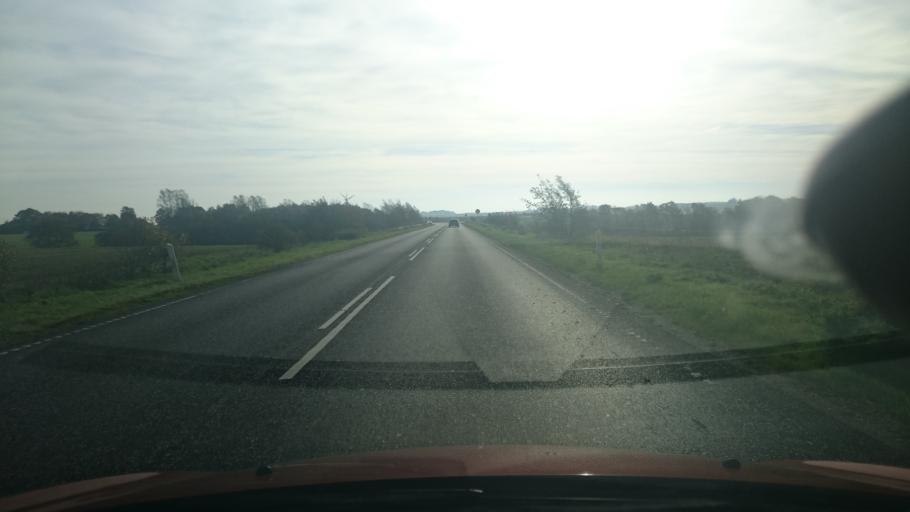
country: DK
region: Central Jutland
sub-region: Randers Kommune
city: Assentoft
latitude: 56.4356
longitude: 10.1294
